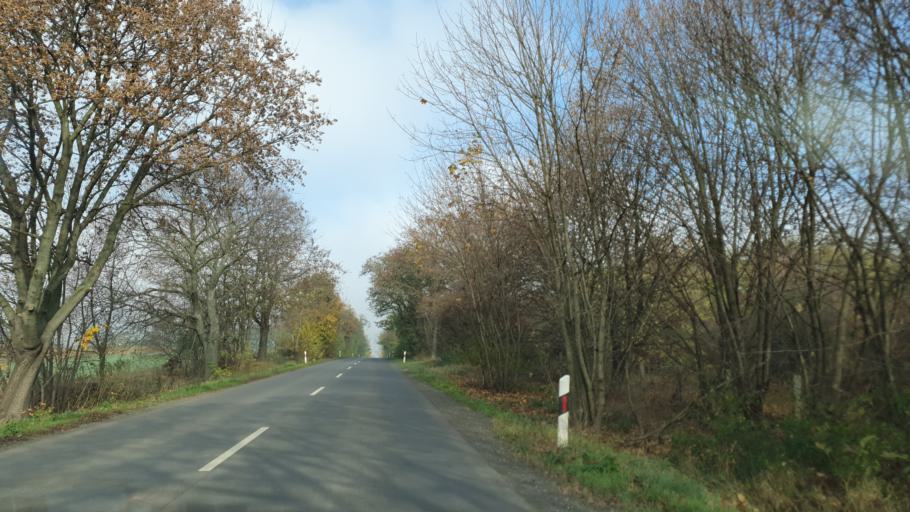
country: HU
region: Pest
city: Orbottyan
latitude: 47.6638
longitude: 19.2385
